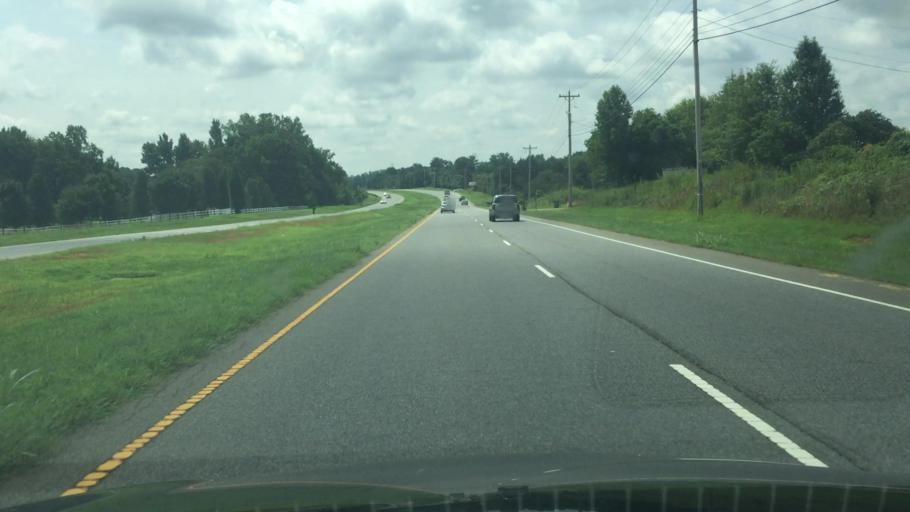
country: US
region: North Carolina
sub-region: Rowan County
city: Enochville
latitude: 35.4802
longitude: -80.6737
